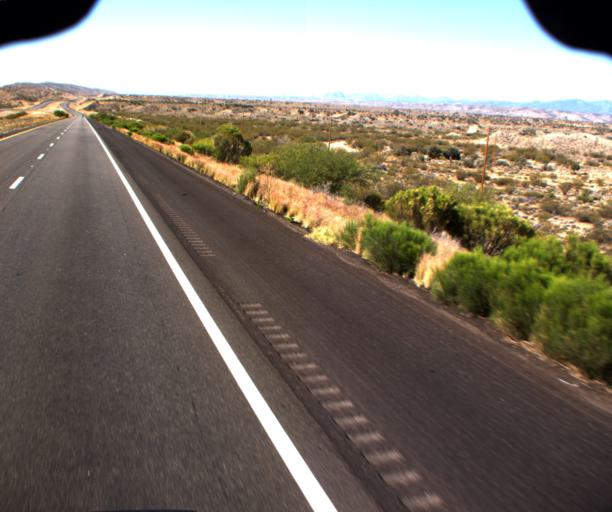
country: US
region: Arizona
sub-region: Mohave County
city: Kingman
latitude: 35.0248
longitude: -113.6649
